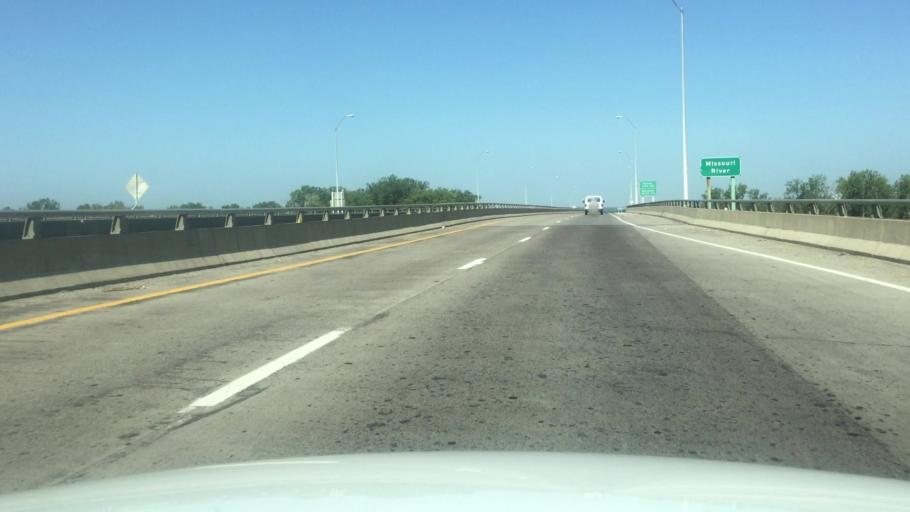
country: US
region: Kansas
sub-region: Doniphan County
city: Elwood
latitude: 39.7486
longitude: -94.8576
